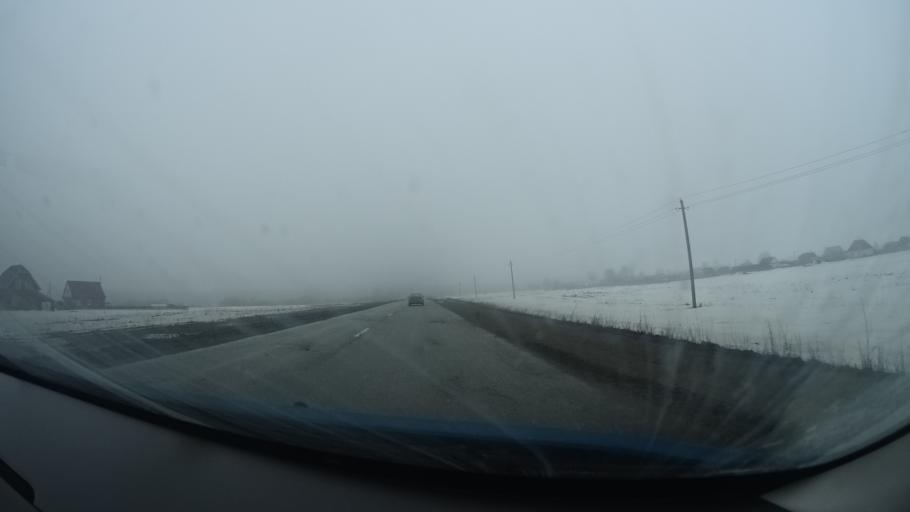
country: RU
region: Perm
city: Kuyeda
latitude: 56.4523
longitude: 55.6113
